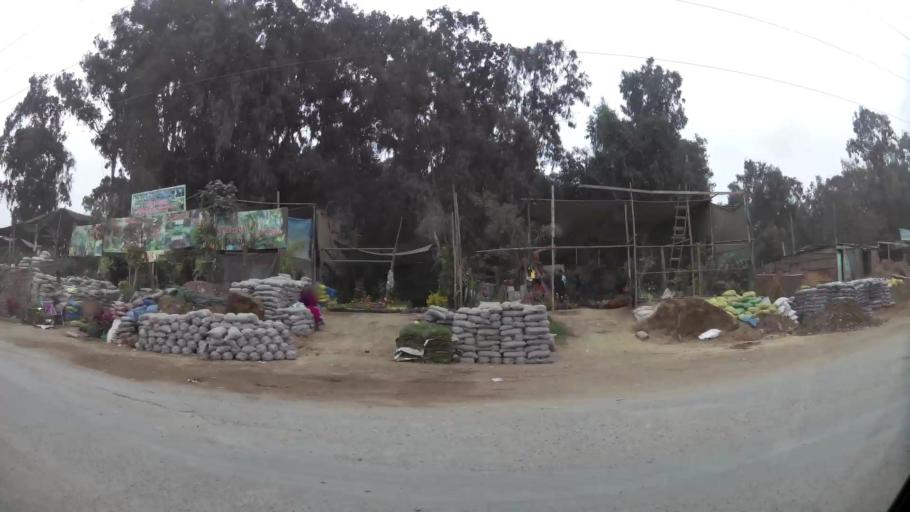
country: PE
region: Lima
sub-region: Lima
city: Surco
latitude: -12.1888
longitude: -76.9726
